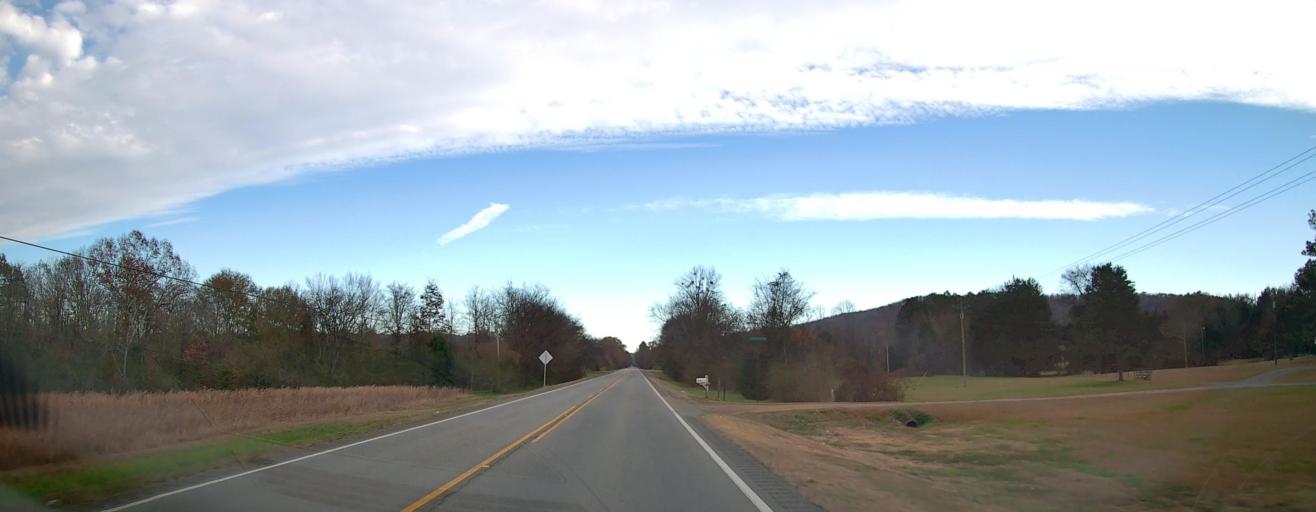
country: US
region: Alabama
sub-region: Marshall County
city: Arab
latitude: 34.3979
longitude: -86.6796
